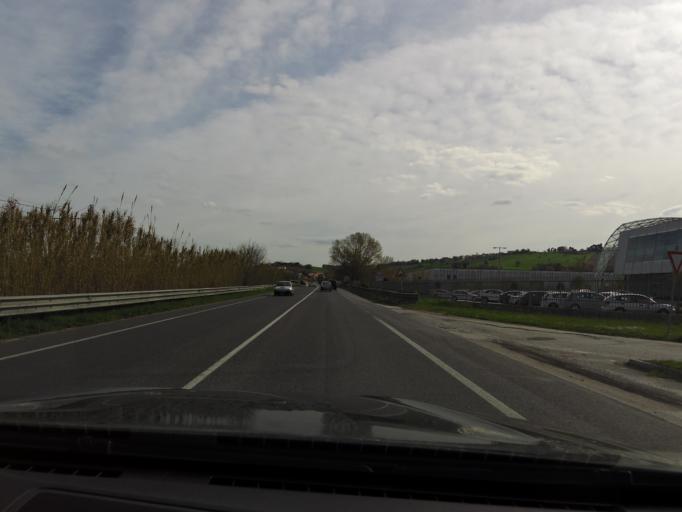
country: IT
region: The Marches
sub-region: Provincia di Ancona
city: Camerano
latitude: 43.5031
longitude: 13.5337
